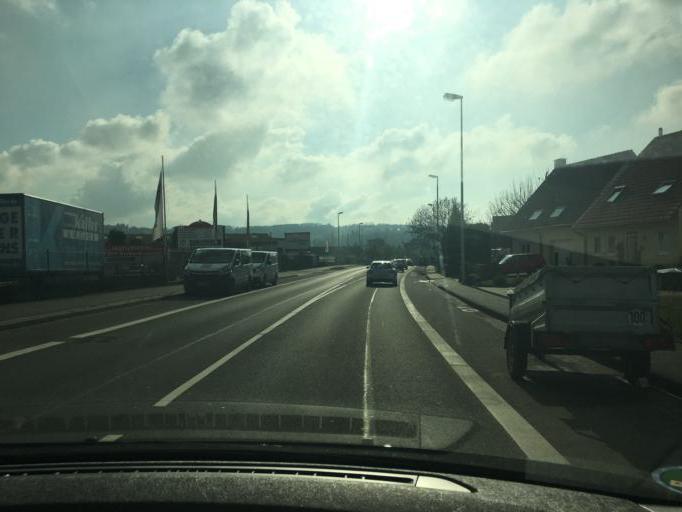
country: DE
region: North Rhine-Westphalia
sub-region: Regierungsbezirk Koln
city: Alfter
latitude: 50.7568
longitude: 7.0167
